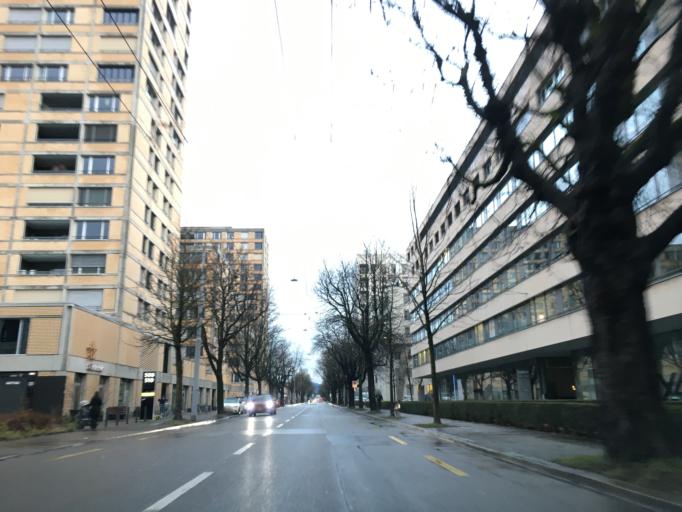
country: CH
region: Zurich
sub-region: Bezirk Zuerich
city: Zuerich (Kreis 9) / Altstetten
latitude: 47.3896
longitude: 8.4931
